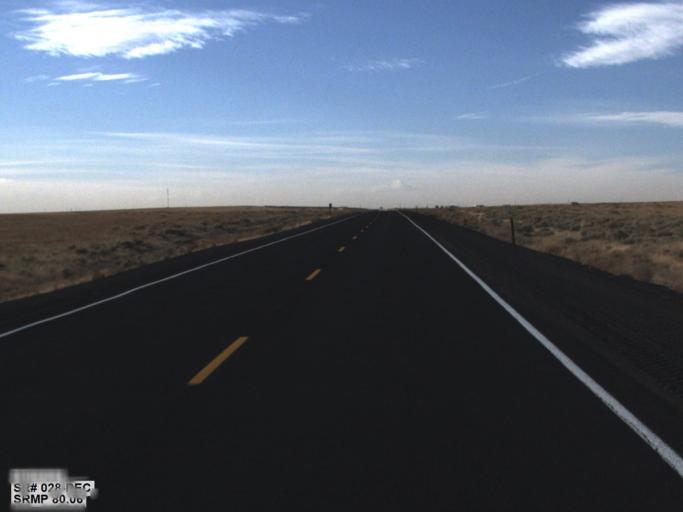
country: US
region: Washington
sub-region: Grant County
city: Moses Lake
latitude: 47.3590
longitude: -118.9599
